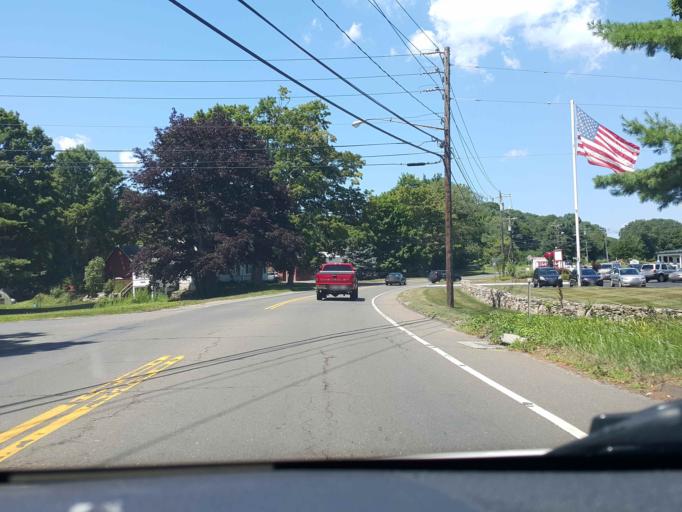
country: US
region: Connecticut
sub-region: New Haven County
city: Guilford
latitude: 41.2889
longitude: -72.6940
